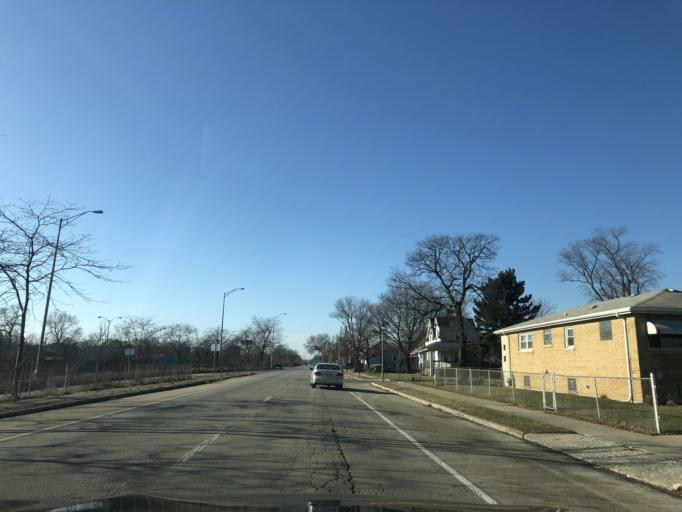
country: US
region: Illinois
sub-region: Cook County
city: Maywood
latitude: 41.8717
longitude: -87.8414
